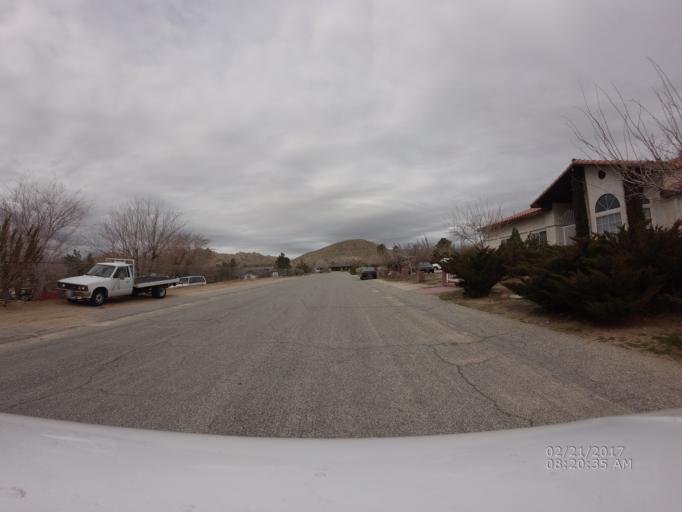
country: US
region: California
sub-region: Los Angeles County
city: Lake Los Angeles
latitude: 34.6014
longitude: -117.8406
